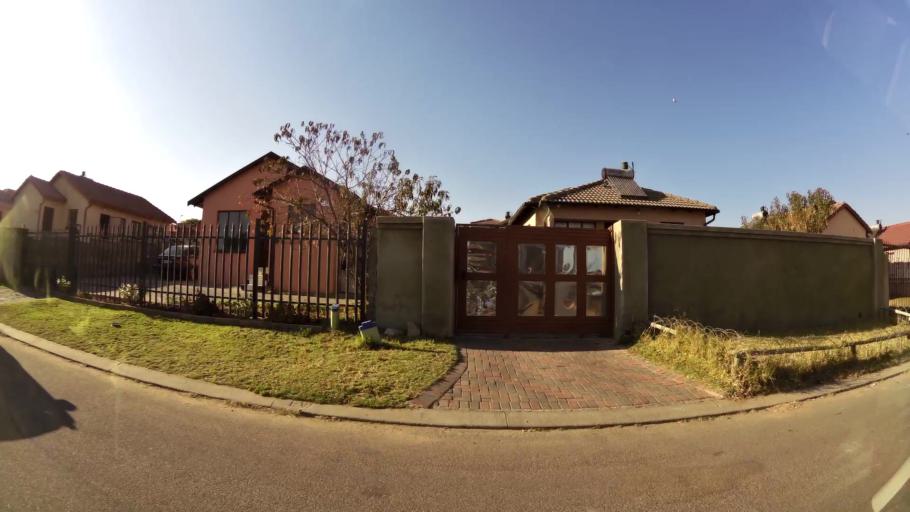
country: ZA
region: Gauteng
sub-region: City of Johannesburg Metropolitan Municipality
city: Modderfontein
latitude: -26.0424
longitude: 28.1598
